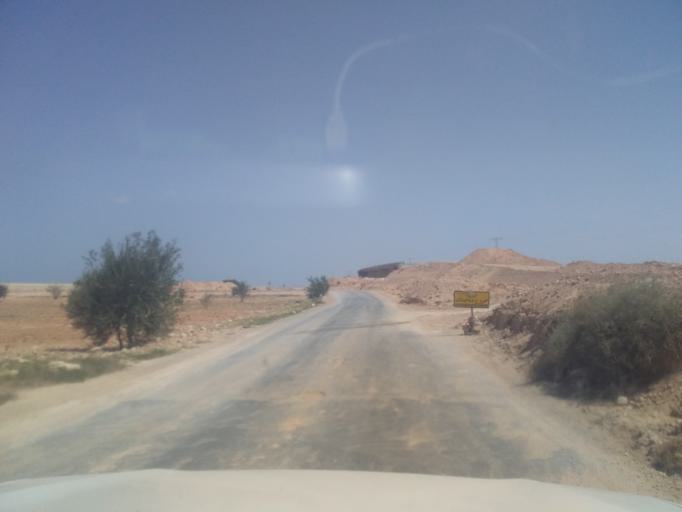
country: TN
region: Qabis
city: Matmata
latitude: 33.6060
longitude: 10.2001
